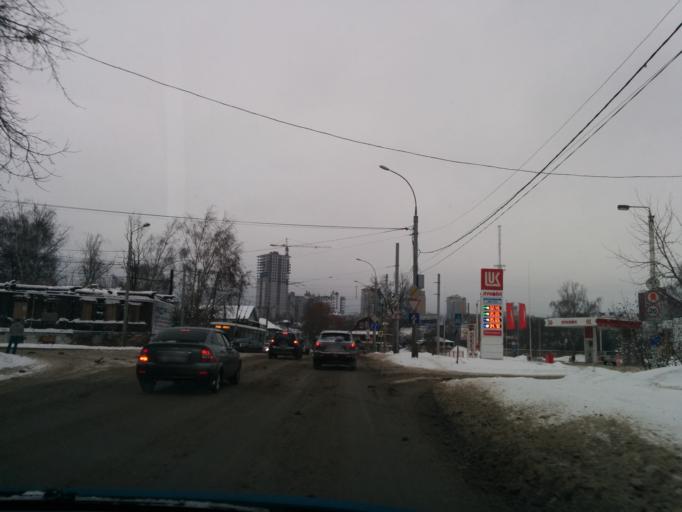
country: RU
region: Perm
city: Perm
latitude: 58.0154
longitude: 56.2638
